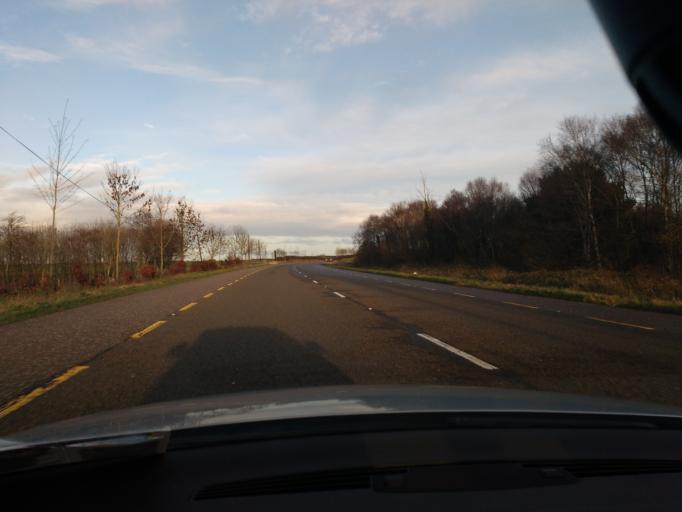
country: IE
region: Munster
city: Thurles
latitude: 52.6876
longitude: -7.6633
